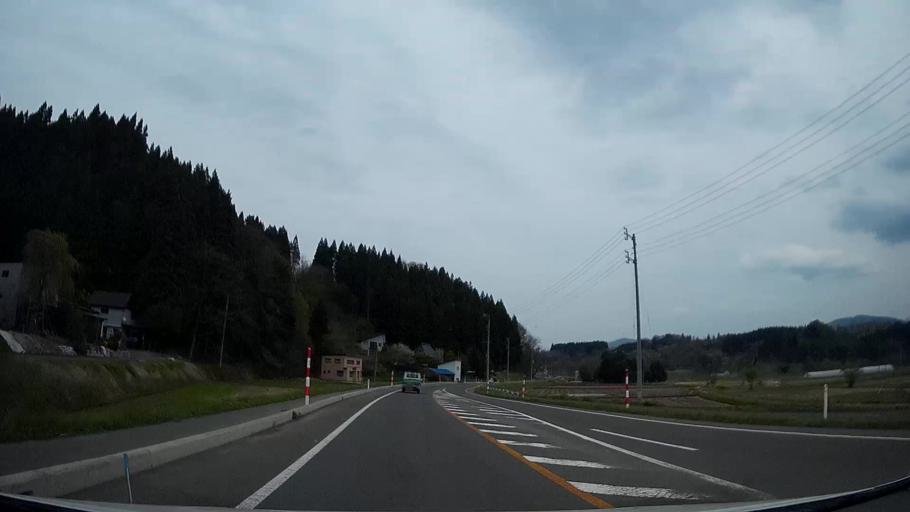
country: JP
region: Akita
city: Hanawa
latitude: 40.2747
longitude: 140.7939
